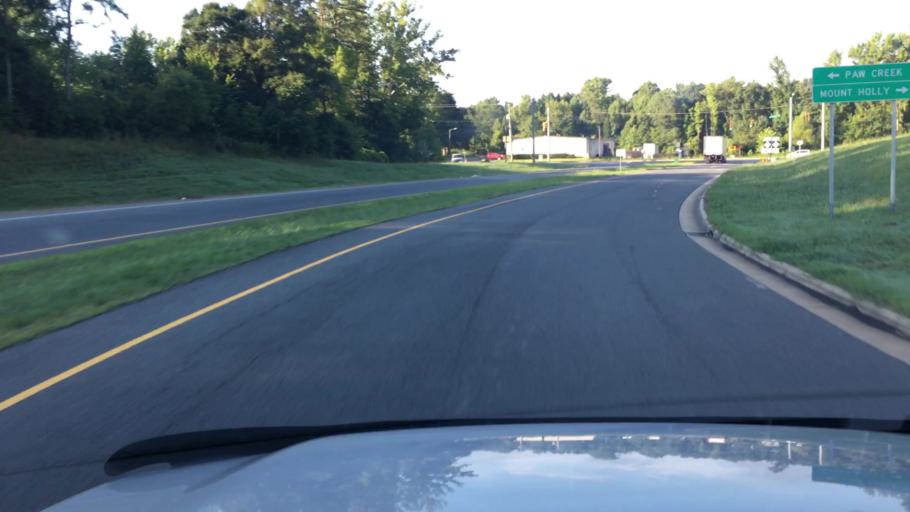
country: US
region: North Carolina
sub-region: Gaston County
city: Mount Holly
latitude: 35.2895
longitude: -80.9620
